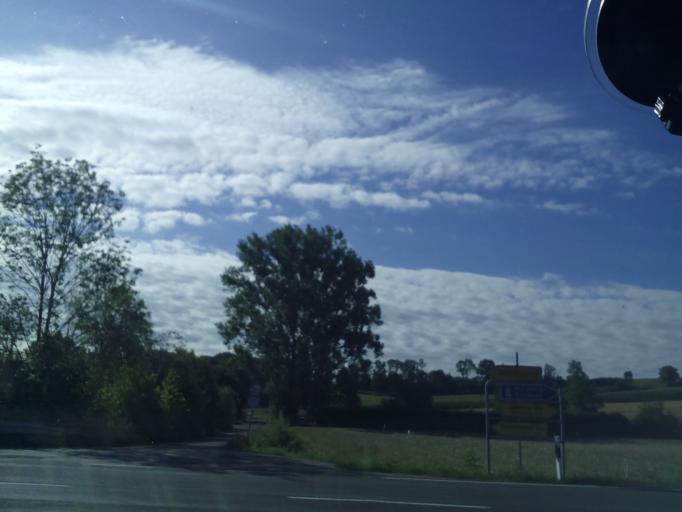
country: DE
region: Bavaria
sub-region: Upper Franconia
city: Buttenheim
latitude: 49.8032
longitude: 11.0433
